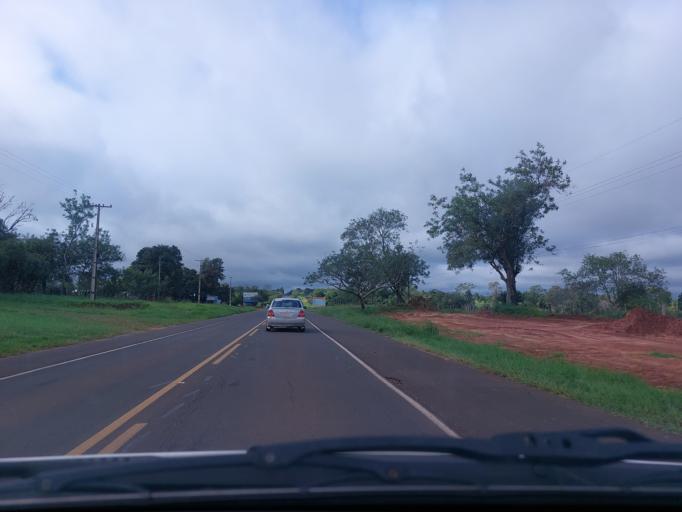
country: PY
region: San Pedro
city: Guayaybi
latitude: -24.5915
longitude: -56.3955
